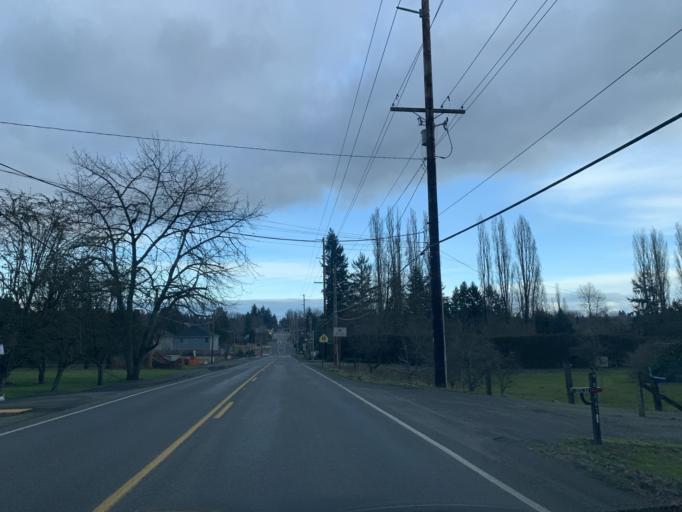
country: US
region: Washington
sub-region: Pierce County
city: Milton
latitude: 47.2355
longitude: -122.3022
